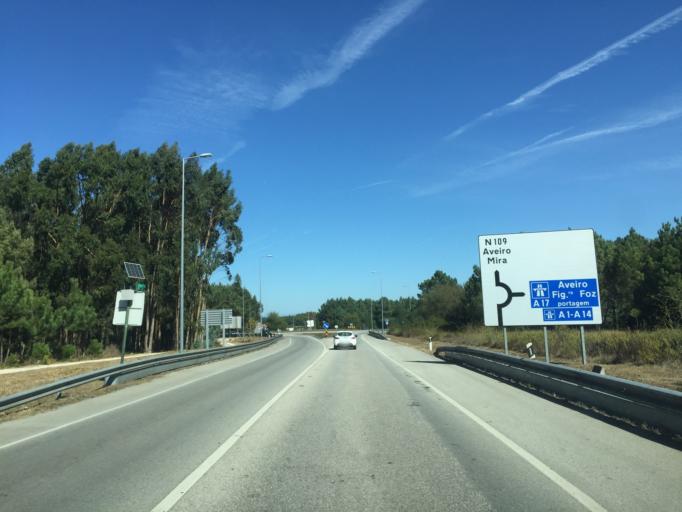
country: PT
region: Coimbra
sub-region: Figueira da Foz
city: Alhadas
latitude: 40.2192
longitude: -8.8094
